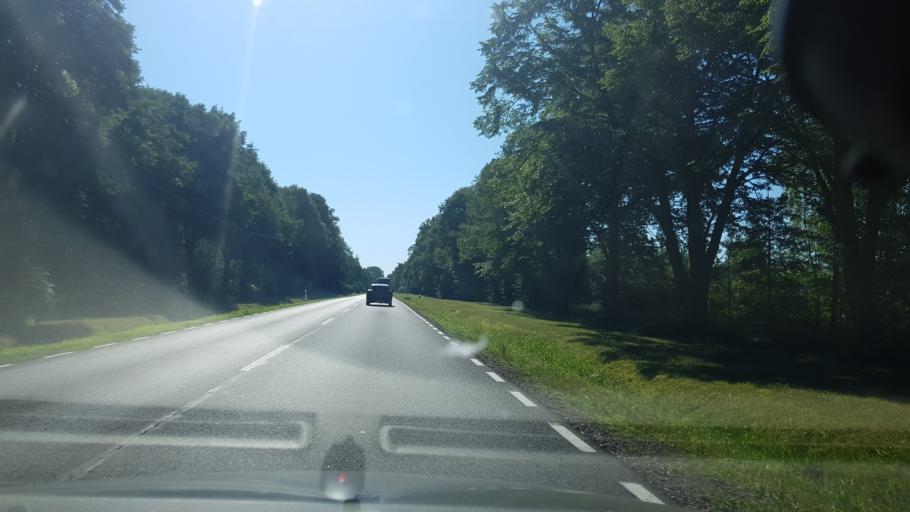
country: PL
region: Masovian Voivodeship
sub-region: Powiat wegrowski
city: Lochow
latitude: 52.5520
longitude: 21.6137
